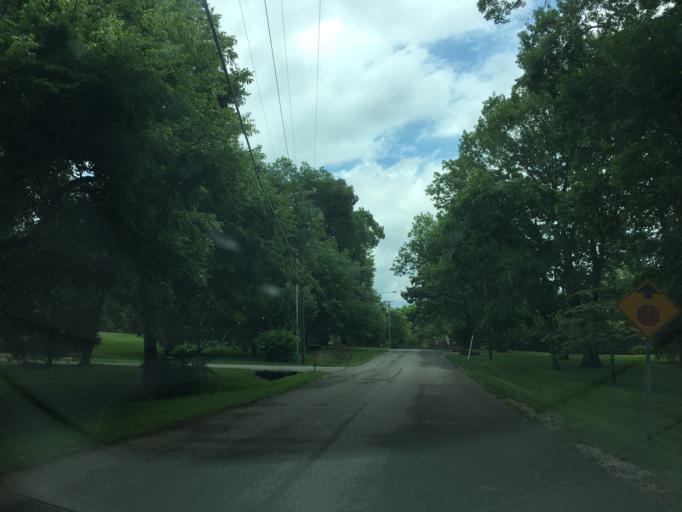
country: US
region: Tennessee
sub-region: Davidson County
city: Belle Meade
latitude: 36.0968
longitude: -86.8451
